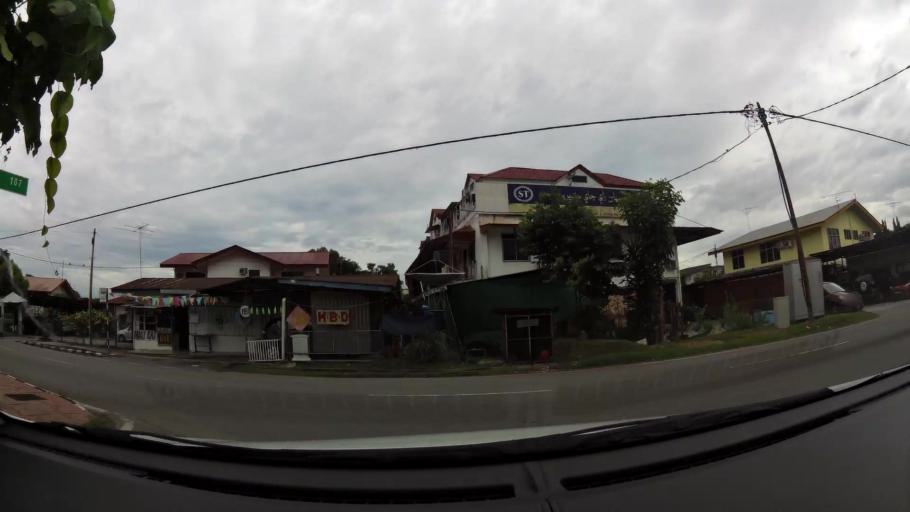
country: BN
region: Brunei and Muara
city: Bandar Seri Begawan
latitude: 4.8960
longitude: 114.9278
